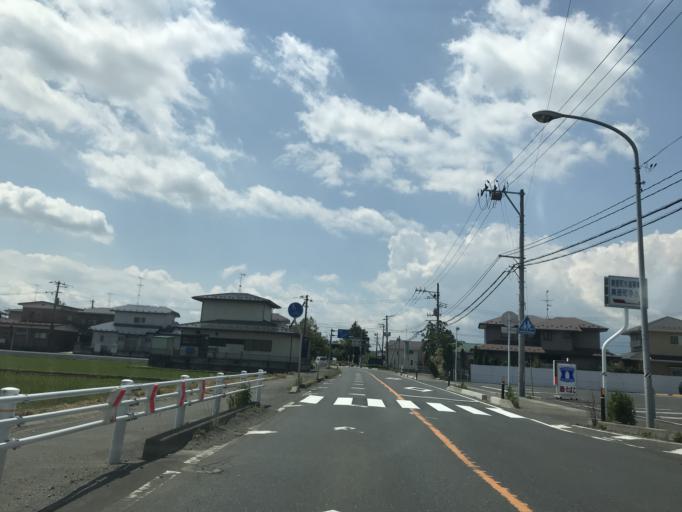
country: JP
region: Miyagi
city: Kogota
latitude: 38.5344
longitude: 141.0546
